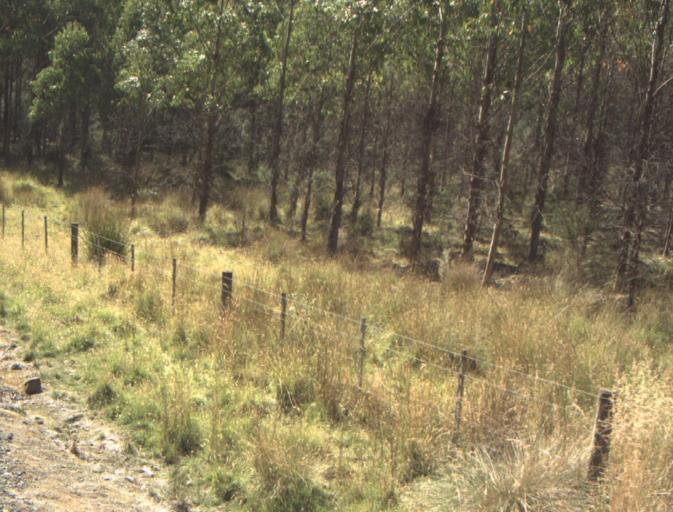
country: AU
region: Tasmania
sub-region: Launceston
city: Newstead
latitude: -41.3062
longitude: 147.3113
